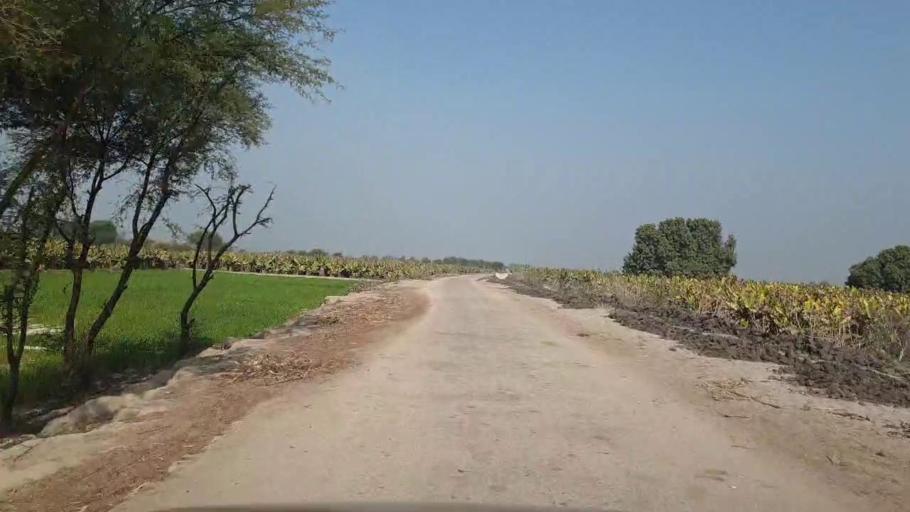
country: PK
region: Sindh
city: Bhit Shah
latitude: 25.7750
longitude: 68.4940
